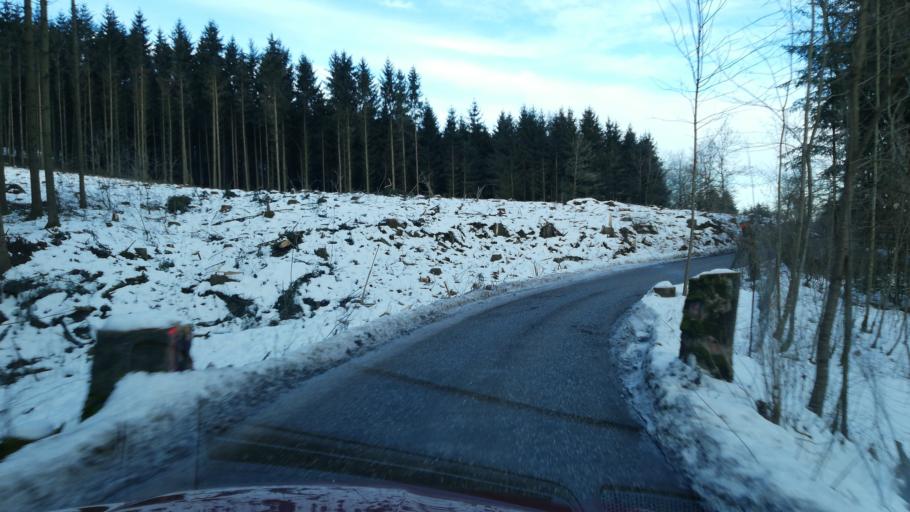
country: AT
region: Upper Austria
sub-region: Wels-Land
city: Buchkirchen
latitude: 48.2363
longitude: 13.9905
